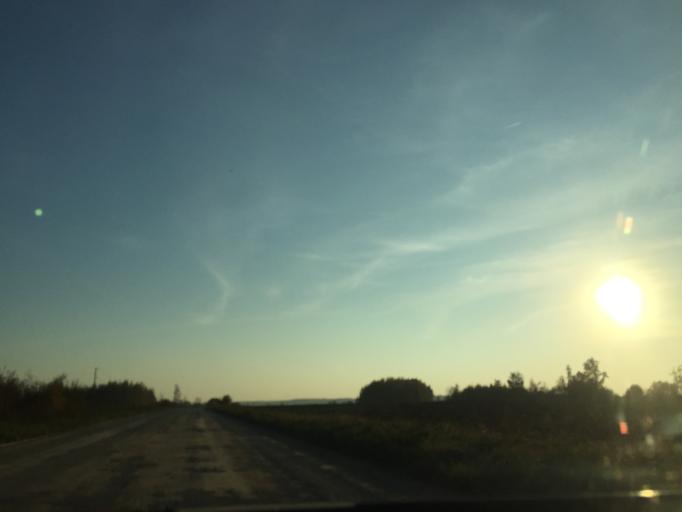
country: LV
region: Vainode
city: Vainode
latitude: 56.5366
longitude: 21.8340
